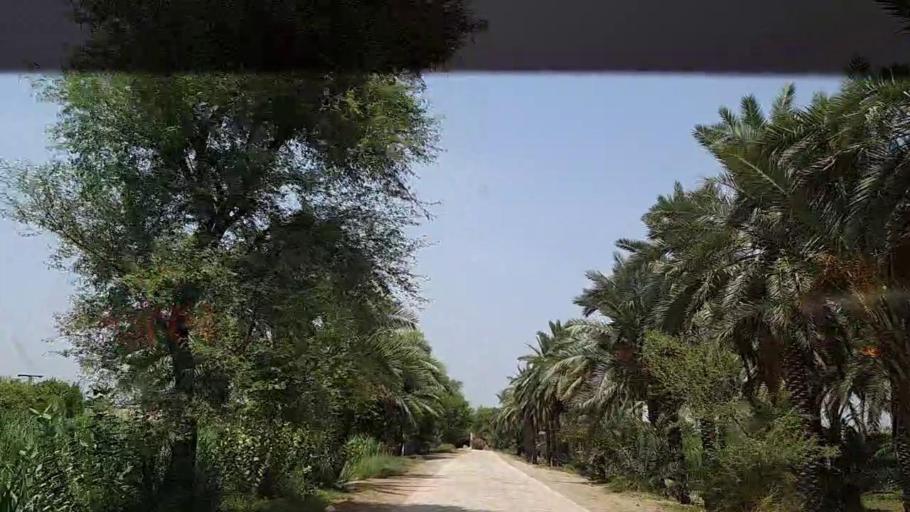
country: PK
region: Sindh
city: Ghotki
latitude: 28.0187
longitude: 69.3538
